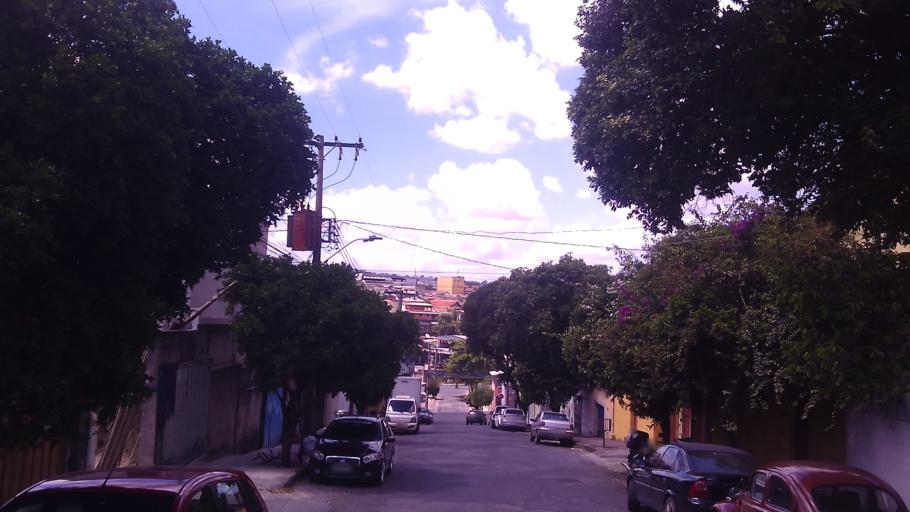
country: BR
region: Minas Gerais
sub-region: Contagem
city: Contagem
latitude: -19.9015
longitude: -44.0093
